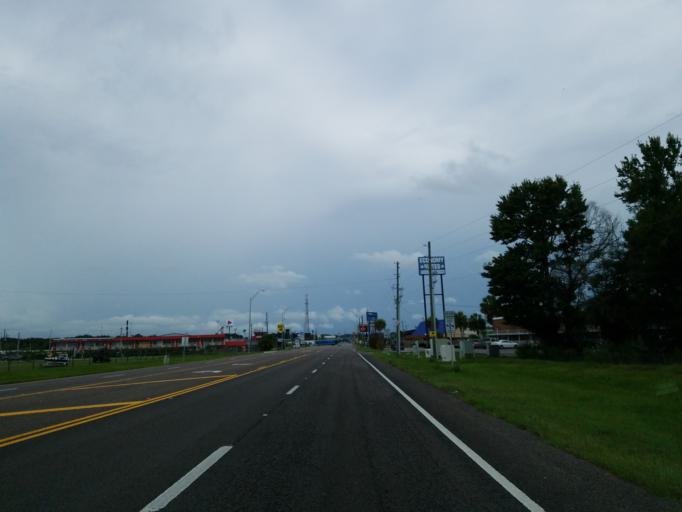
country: US
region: Florida
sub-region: Sumter County
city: Wildwood
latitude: 28.8756
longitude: -82.0996
